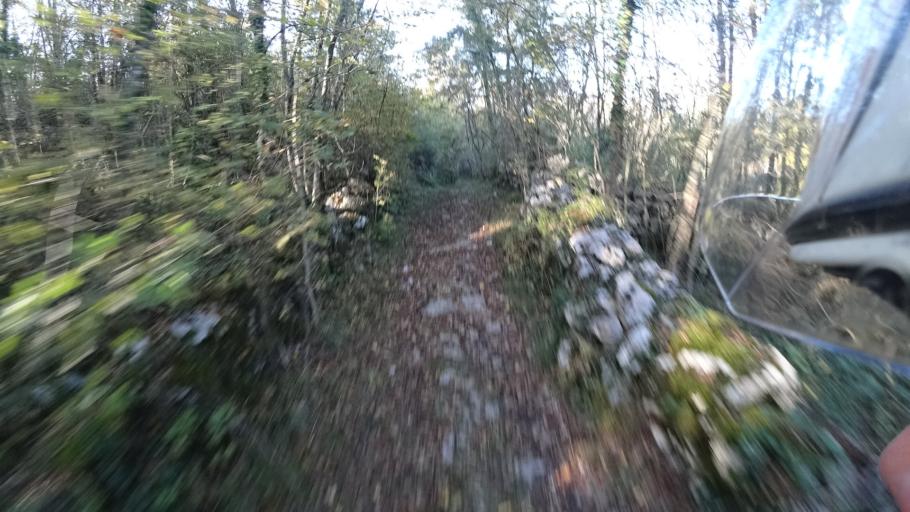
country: HR
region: Primorsko-Goranska
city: Matulji
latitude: 45.4055
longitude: 14.2859
